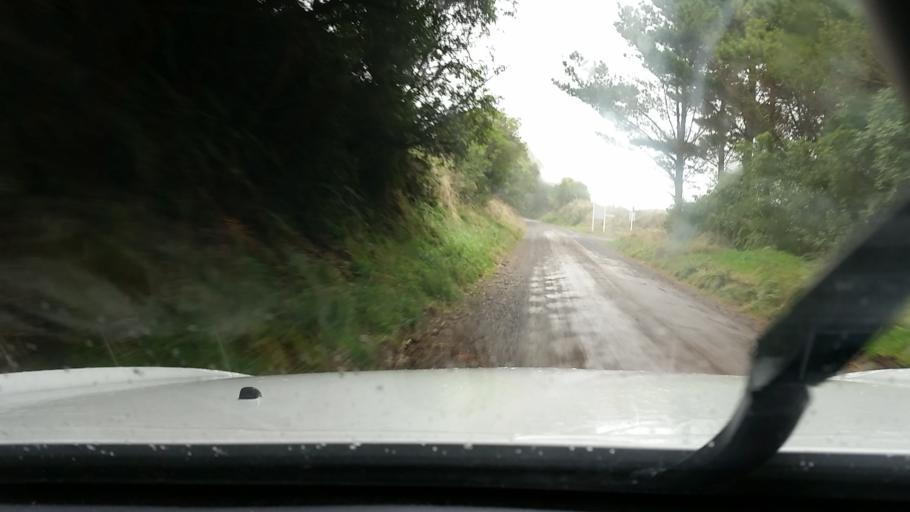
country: NZ
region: Bay of Plenty
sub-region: Rotorua District
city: Rotorua
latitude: -38.2404
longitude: 176.3471
